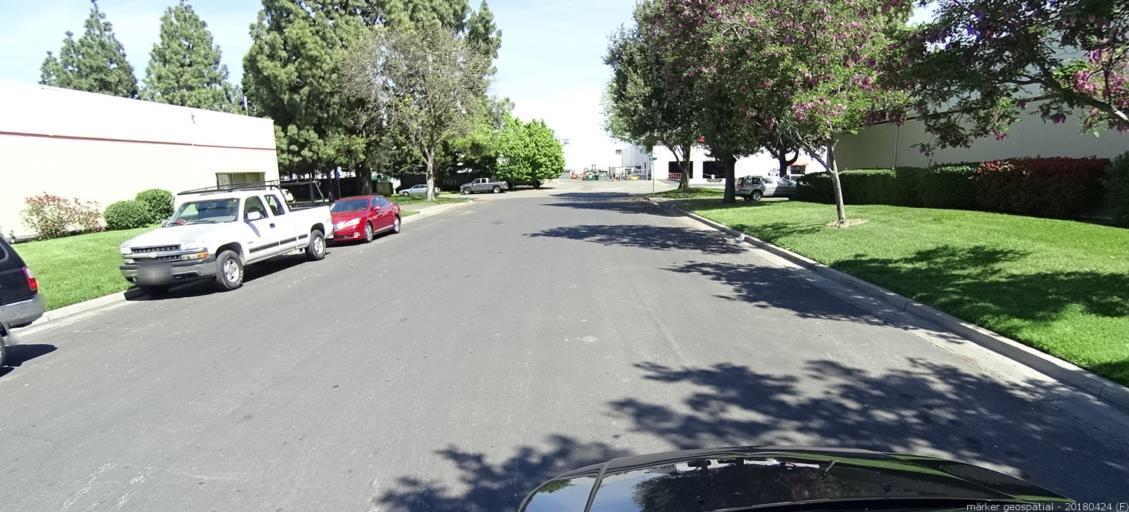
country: US
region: California
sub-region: Yolo County
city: West Sacramento
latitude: 38.5721
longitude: -121.5450
